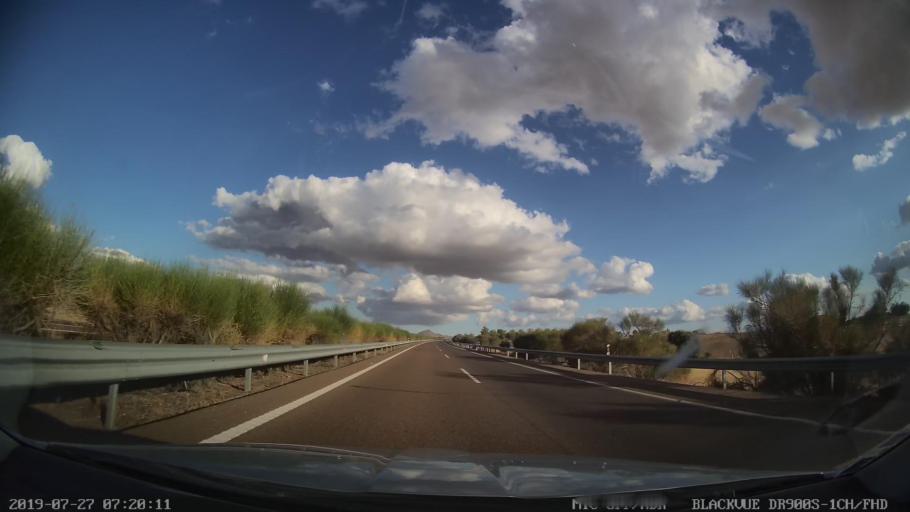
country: ES
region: Extremadura
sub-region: Provincia de Caceres
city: Santa Cruz de la Sierra
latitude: 39.3858
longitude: -5.8842
